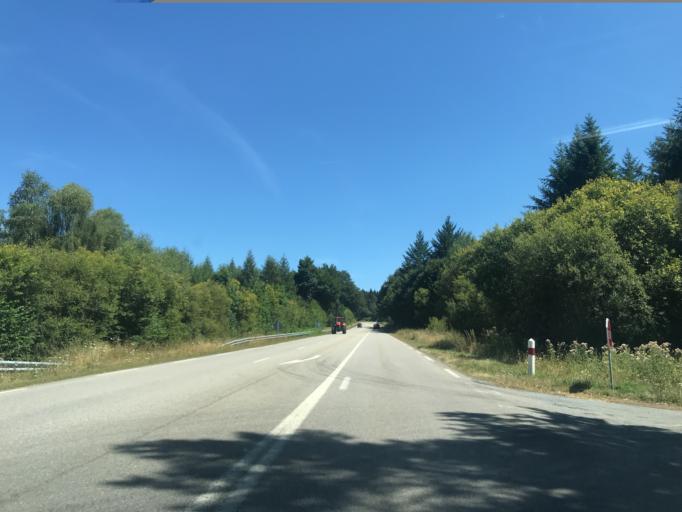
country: FR
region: Limousin
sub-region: Departement de la Correze
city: Meymac
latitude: 45.4775
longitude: 2.1836
